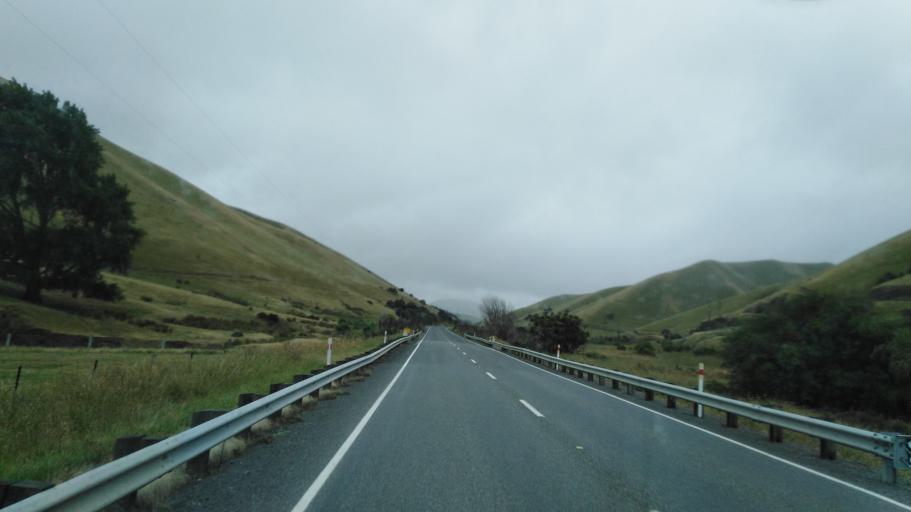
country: NZ
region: Marlborough
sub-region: Marlborough District
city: Blenheim
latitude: -41.6306
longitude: 174.0662
